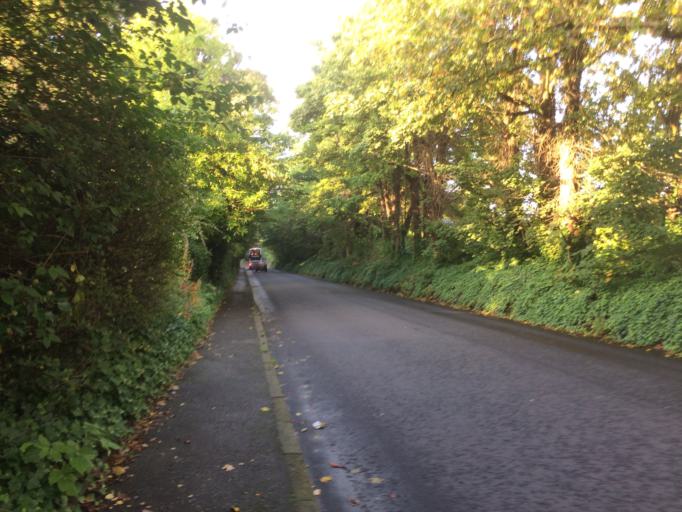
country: GB
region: Scotland
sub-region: Edinburgh
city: Colinton
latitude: 55.9170
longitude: -3.2225
